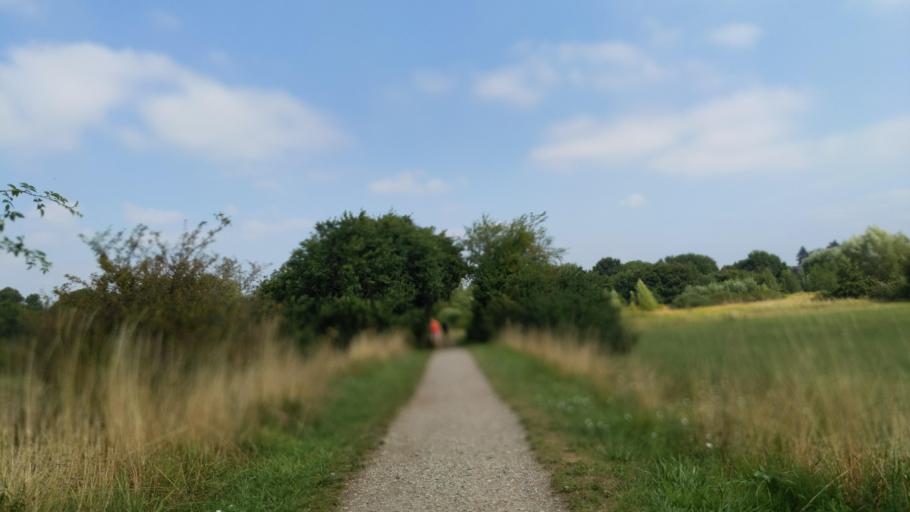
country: DE
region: Schleswig-Holstein
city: Stockelsdorf
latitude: 53.8799
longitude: 10.6330
